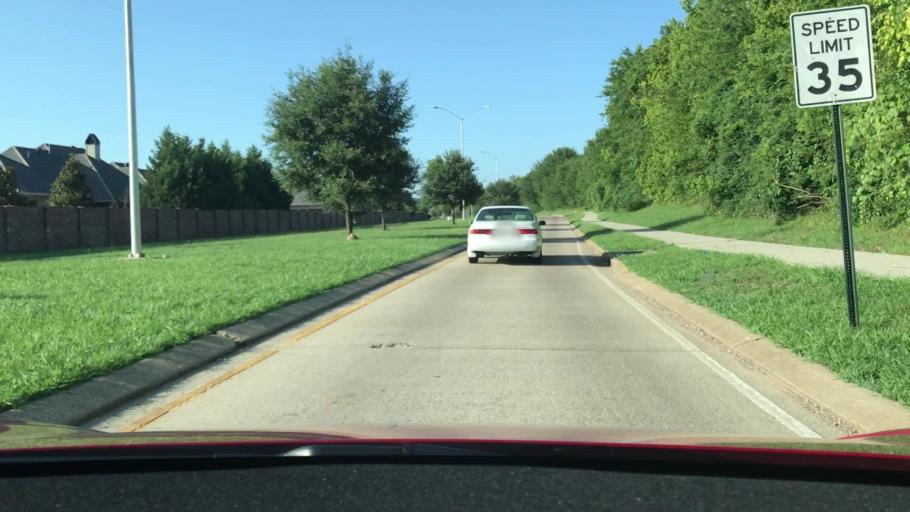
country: US
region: Louisiana
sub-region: Bossier Parish
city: Bossier City
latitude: 32.4500
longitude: -93.7307
